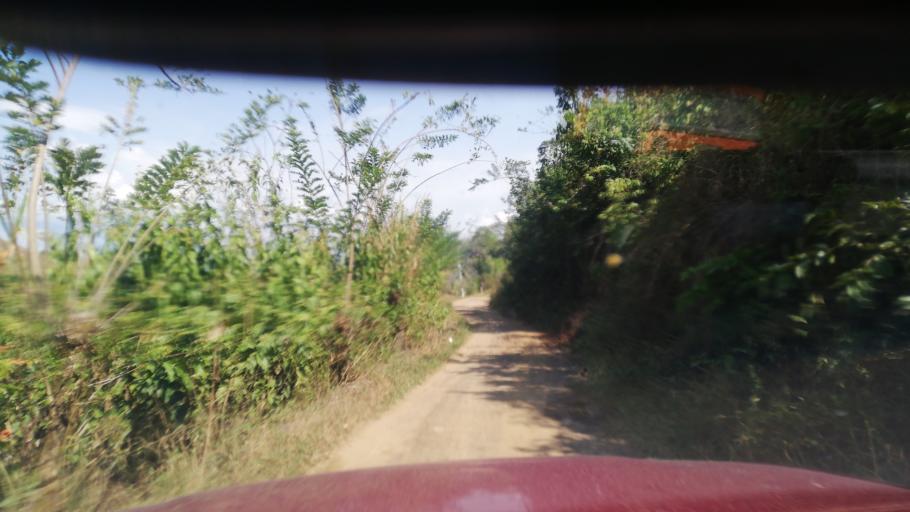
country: CO
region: Risaralda
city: La Virginia
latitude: 4.9013
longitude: -75.9343
